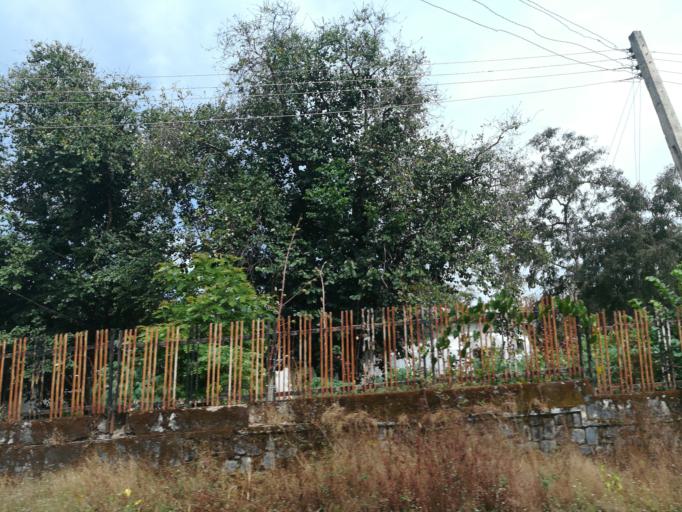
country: NG
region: Plateau
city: Jos
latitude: 9.9053
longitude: 8.8808
